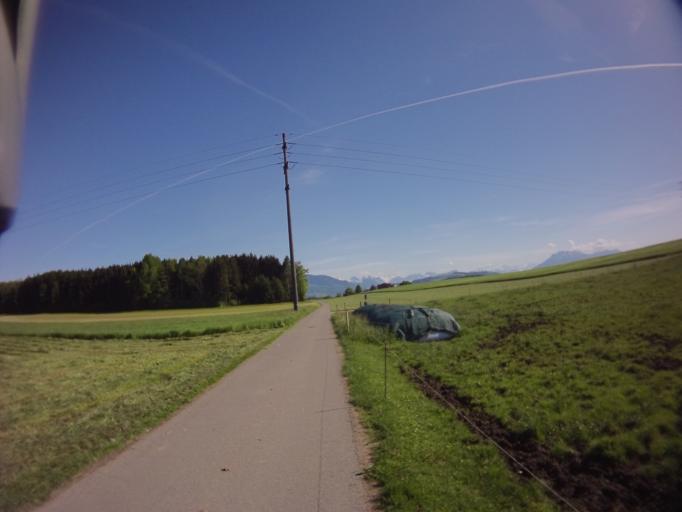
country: CH
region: Zurich
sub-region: Bezirk Affoltern
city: Knonau
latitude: 47.2038
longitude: 8.4482
